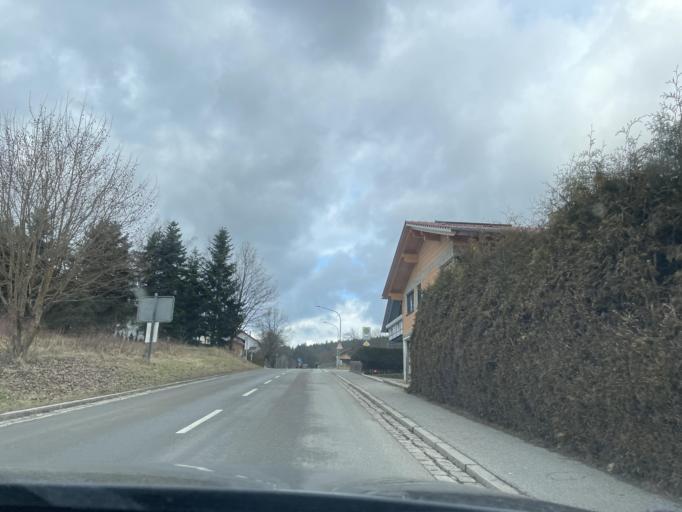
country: DE
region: Bavaria
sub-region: Upper Palatinate
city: Blaibach
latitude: 49.1701
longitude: 12.8048
